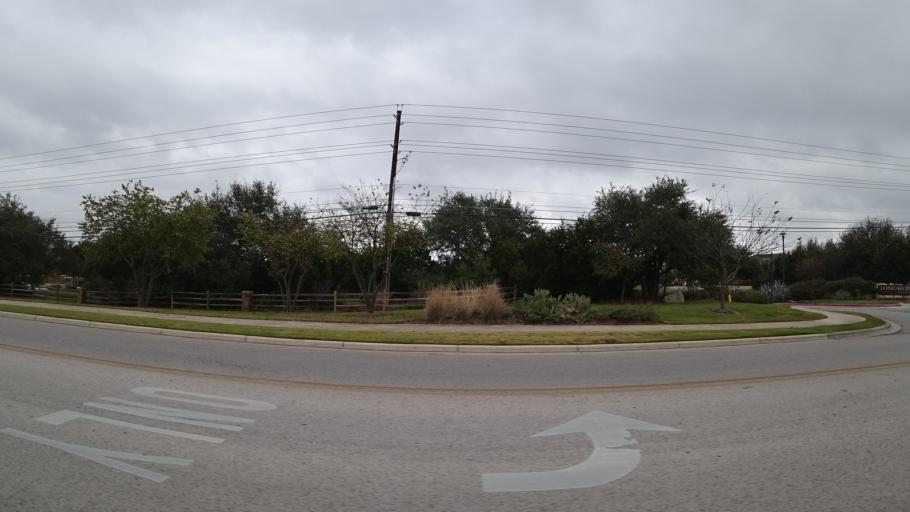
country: US
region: Texas
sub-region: Travis County
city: Bee Cave
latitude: 30.3527
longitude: -97.9113
